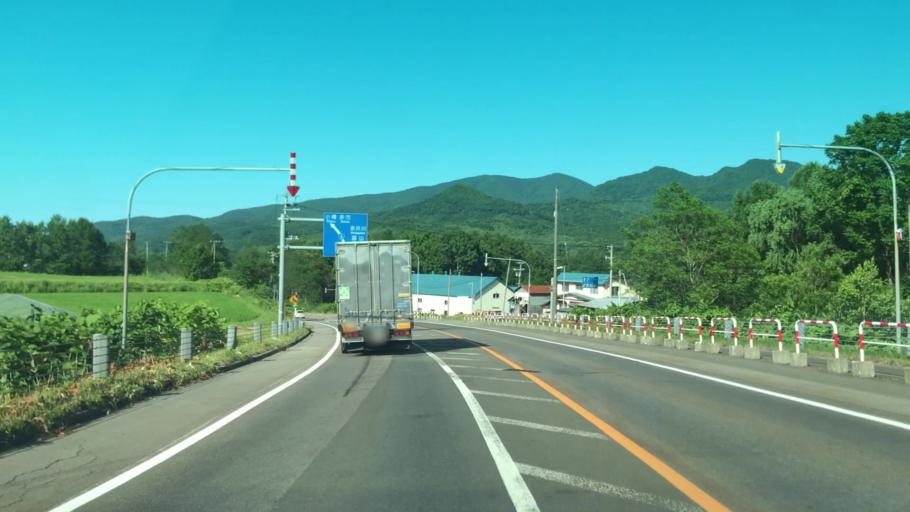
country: JP
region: Hokkaido
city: Yoichi
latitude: 43.0750
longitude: 140.7095
